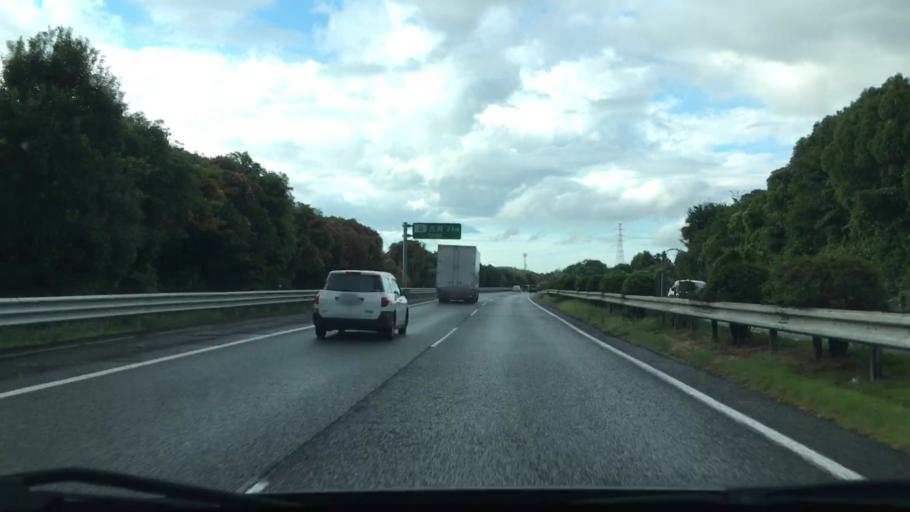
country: JP
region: Fukuoka
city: Koga
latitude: 33.7002
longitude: 130.4852
